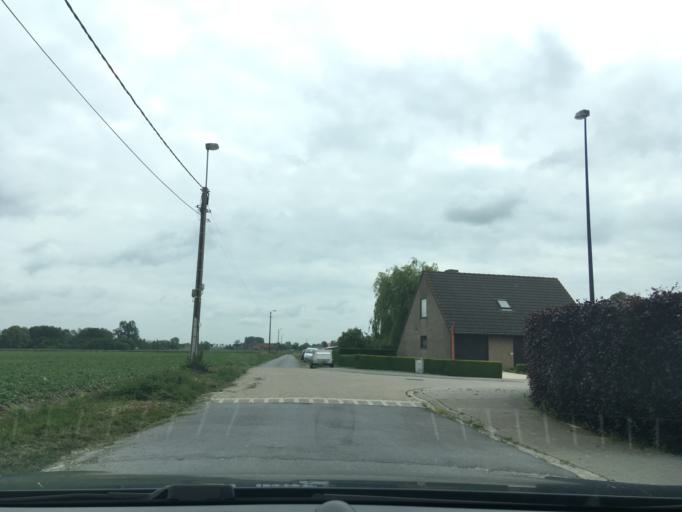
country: BE
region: Flanders
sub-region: Provincie West-Vlaanderen
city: Moorslede
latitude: 50.8699
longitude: 3.0879
